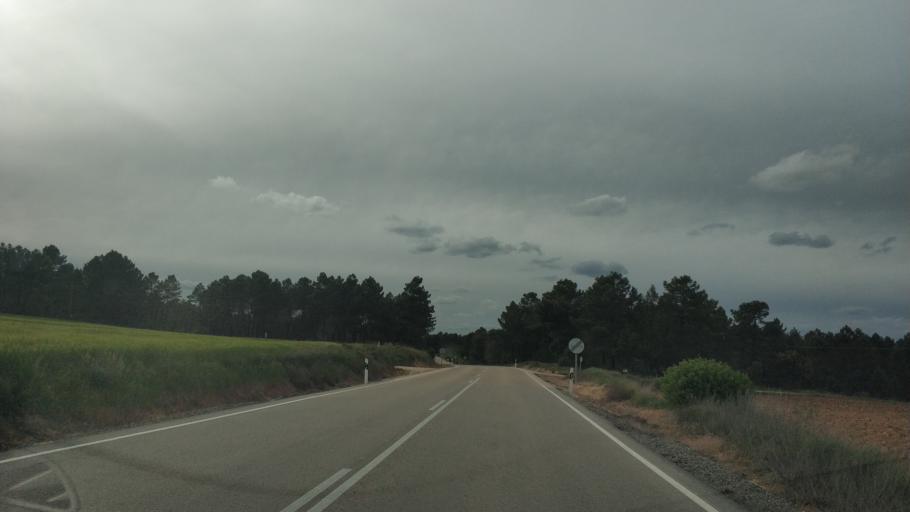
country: ES
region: Castille and Leon
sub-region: Provincia de Soria
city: Valdenebro
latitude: 41.5554
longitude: -2.9652
